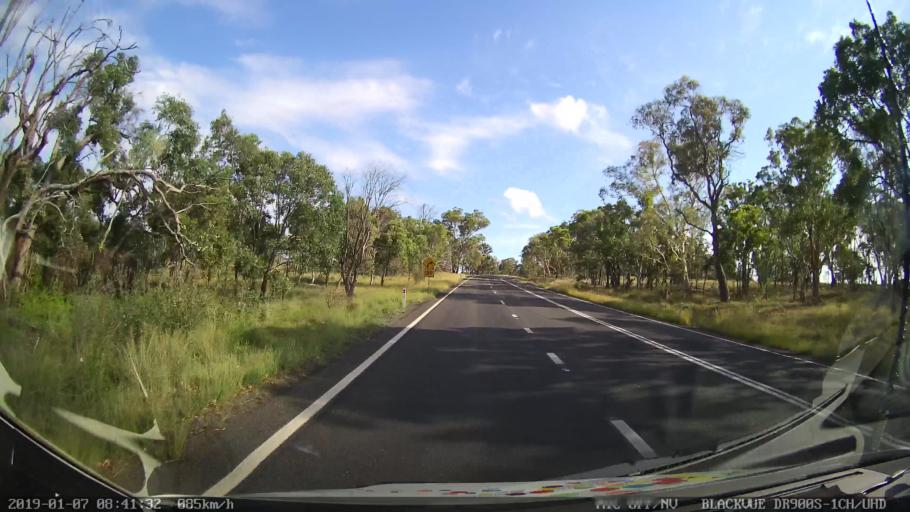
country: AU
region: New South Wales
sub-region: Tamworth Municipality
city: Kootingal
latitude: -30.8664
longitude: 151.2037
